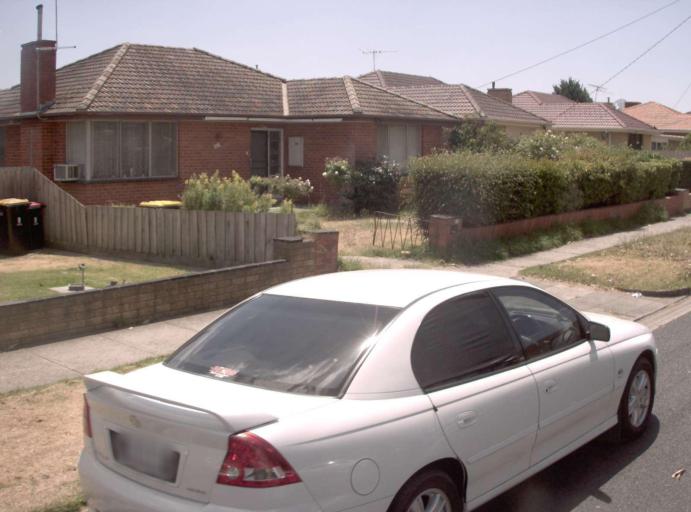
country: AU
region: Victoria
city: Highett
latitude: -37.9424
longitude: 145.0600
